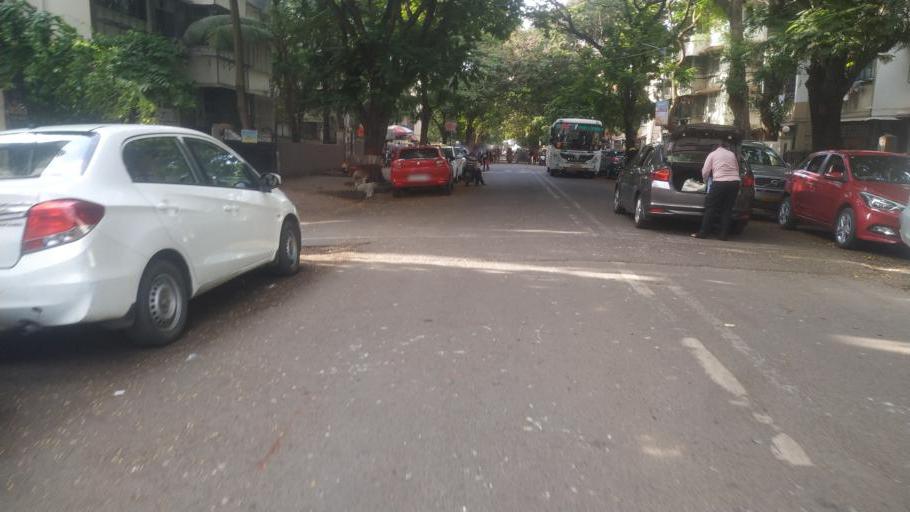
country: IN
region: Maharashtra
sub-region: Mumbai Suburban
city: Mumbai
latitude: 19.0212
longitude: 72.8598
